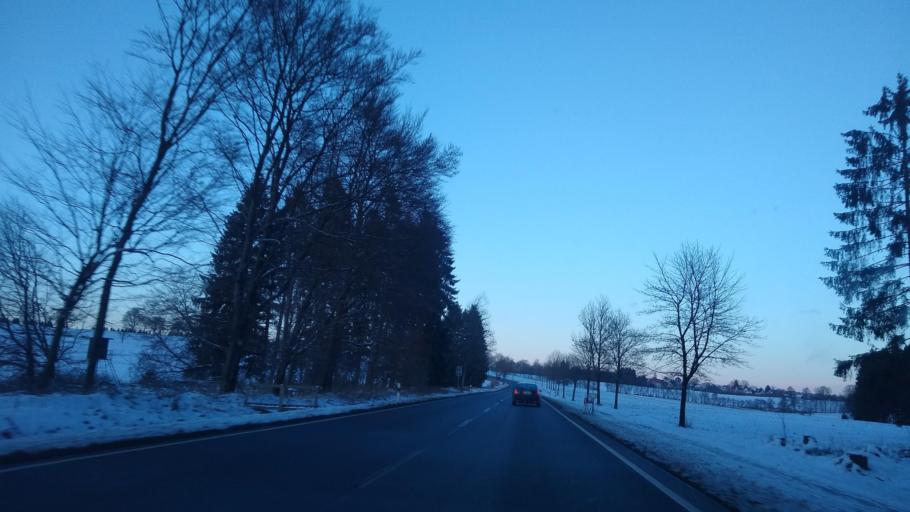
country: DE
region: Lower Saxony
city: Clausthal-Zellerfeld
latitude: 51.7874
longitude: 10.3254
